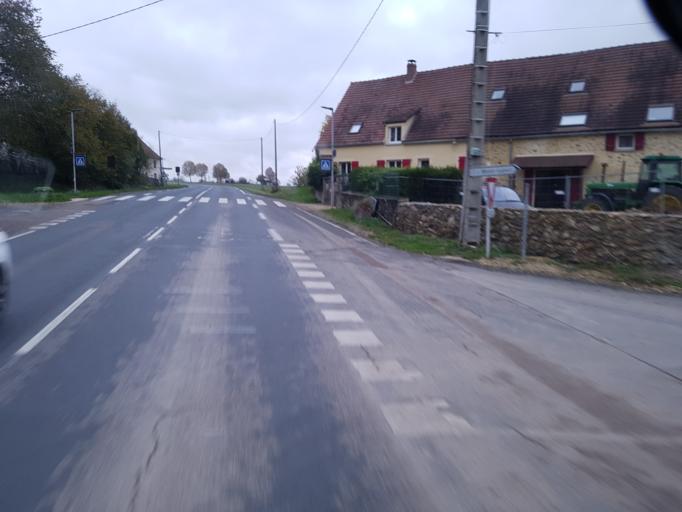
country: FR
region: Champagne-Ardenne
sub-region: Departement de la Marne
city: Montmirail
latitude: 48.8843
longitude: 3.5262
